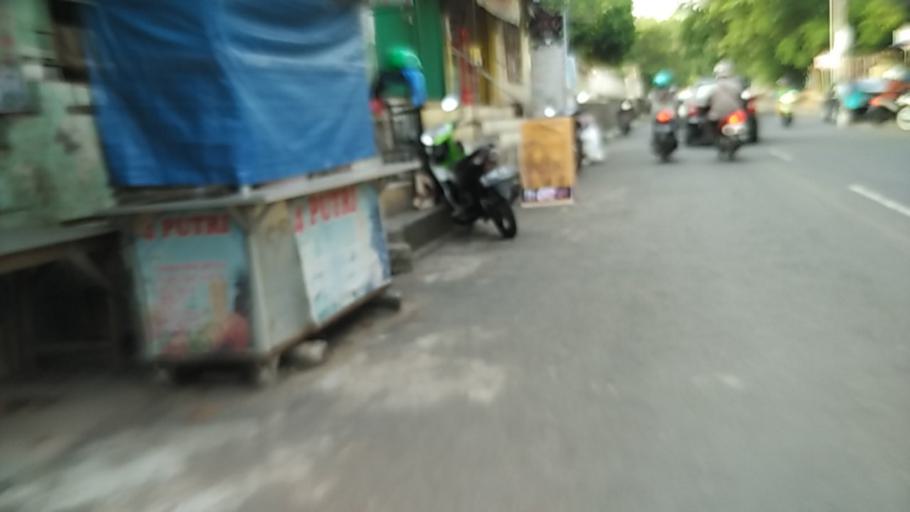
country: ID
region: Central Java
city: Semarang
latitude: -6.9923
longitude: 110.4138
